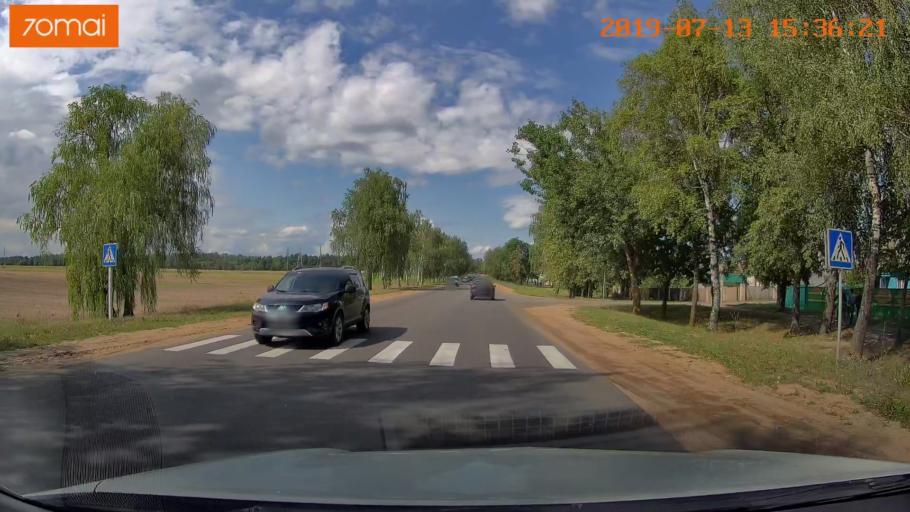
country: BY
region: Mogilev
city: Babruysk
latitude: 53.1307
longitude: 29.1666
